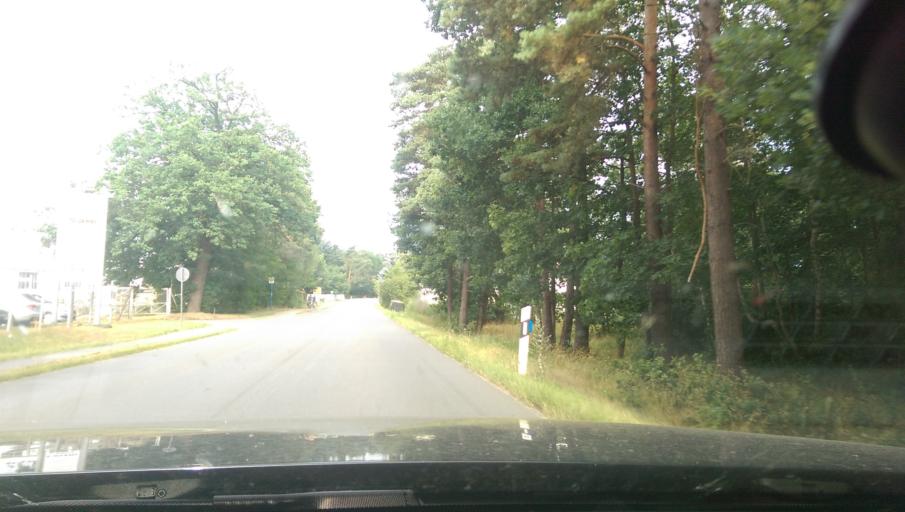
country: DE
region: Lower Saxony
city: Winsen (Aller)
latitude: 52.6717
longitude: 9.8746
